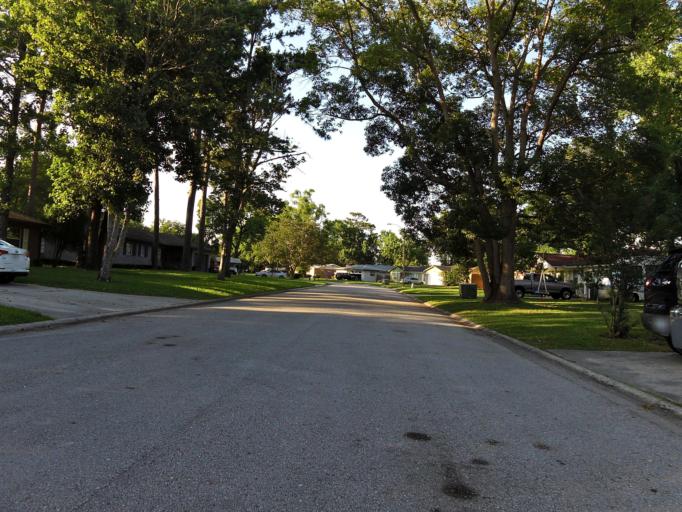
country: US
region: Florida
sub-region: Duval County
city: Jacksonville
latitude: 30.2353
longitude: -81.6032
